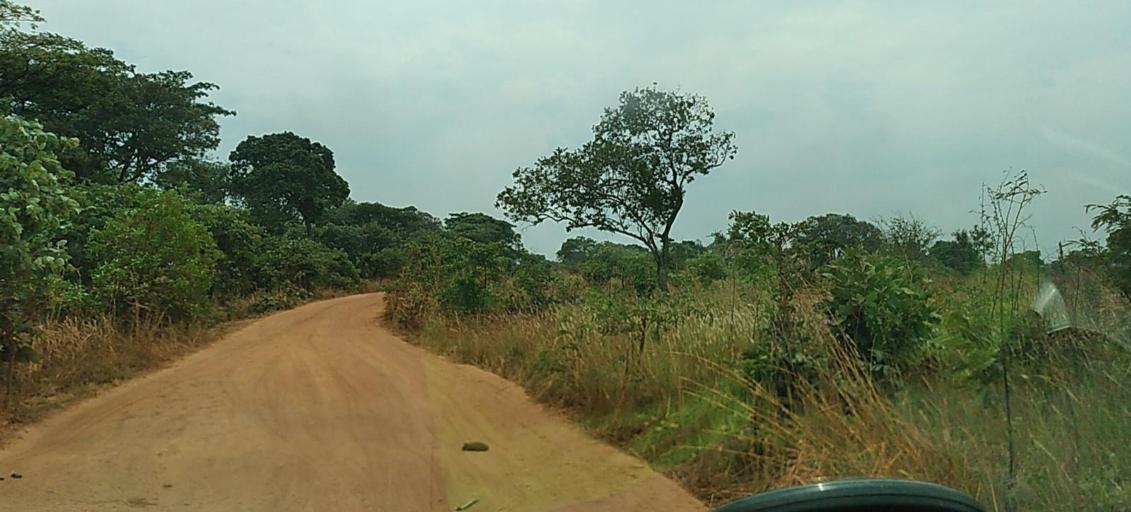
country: ZM
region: North-Western
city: Kansanshi
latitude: -12.0447
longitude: 26.3328
